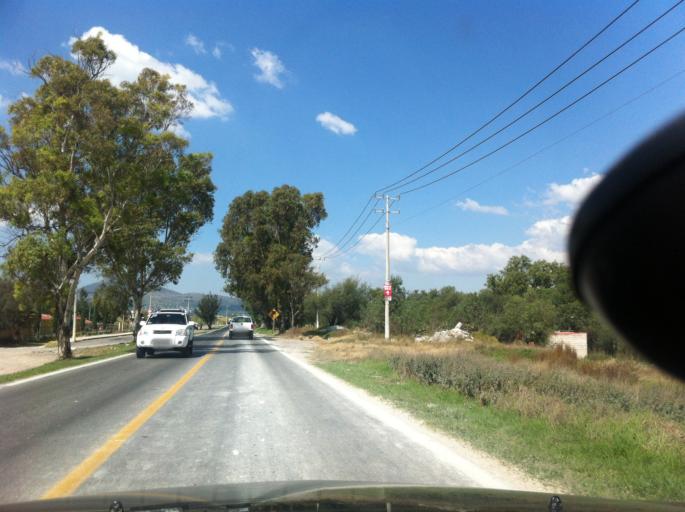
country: MX
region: Mexico
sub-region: Zumpango
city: Zumpango
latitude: 19.7754
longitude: -99.1193
